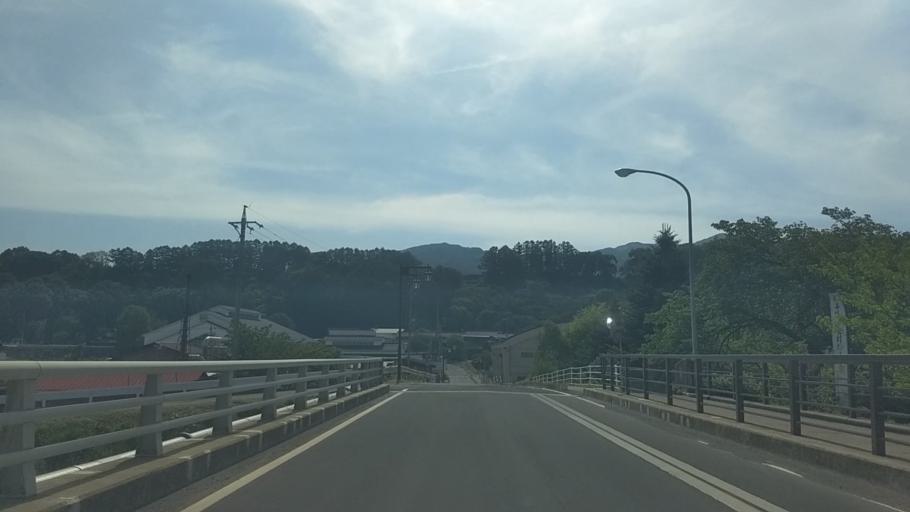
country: JP
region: Nagano
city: Saku
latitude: 36.1371
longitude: 138.4741
